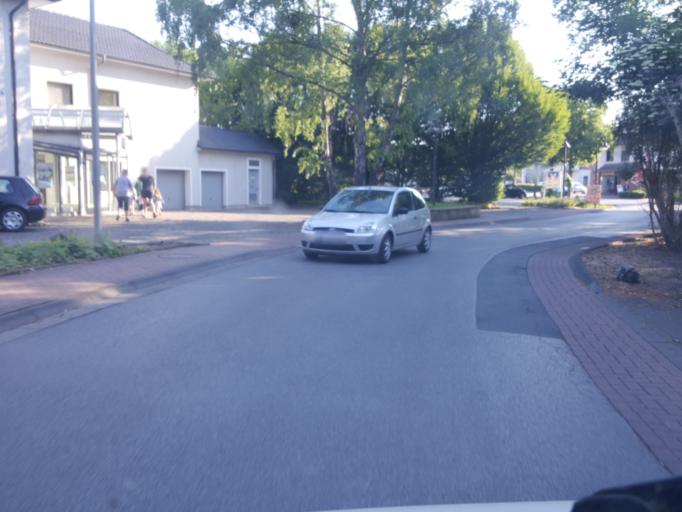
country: DE
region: North Rhine-Westphalia
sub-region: Regierungsbezirk Detmold
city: Hille
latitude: 52.3348
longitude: 8.7442
